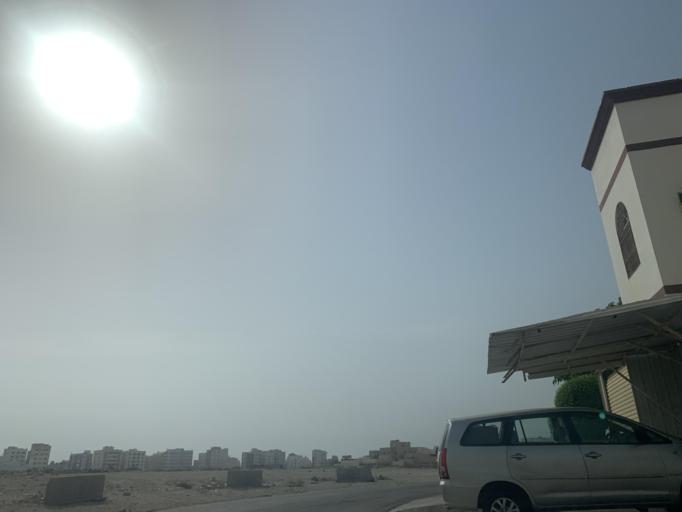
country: BH
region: Northern
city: Madinat `Isa
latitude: 26.1853
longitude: 50.4874
